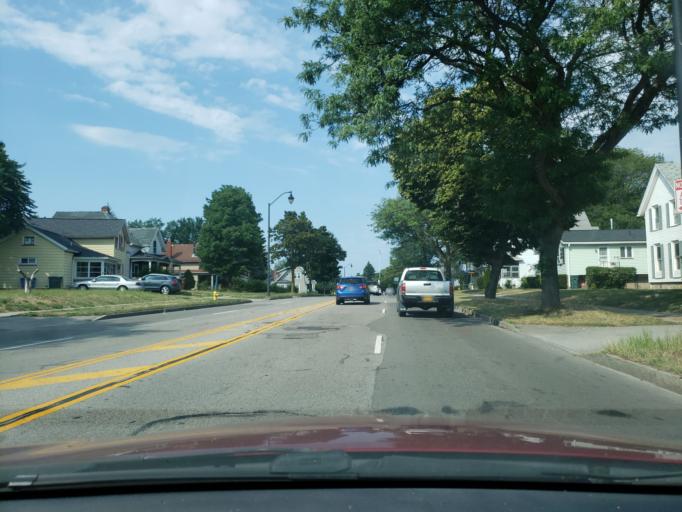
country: US
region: New York
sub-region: Monroe County
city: Irondequoit
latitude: 43.2422
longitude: -77.6199
